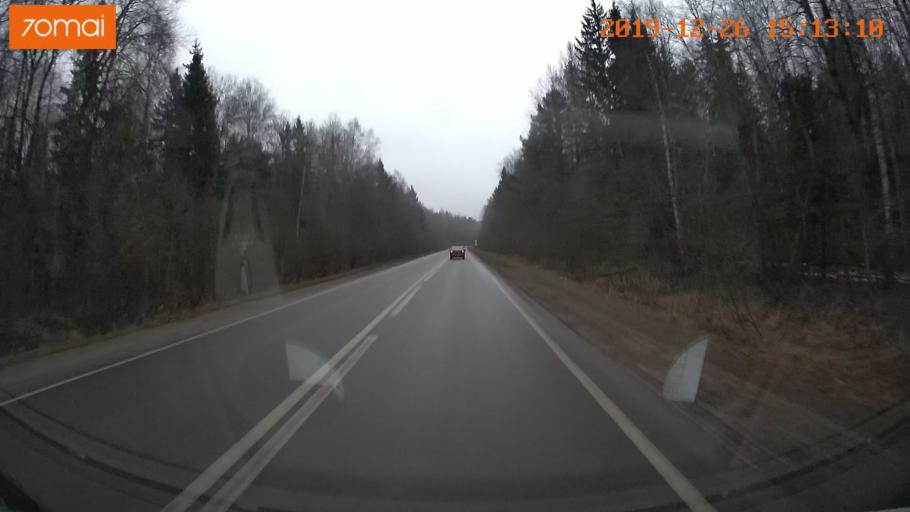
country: RU
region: Jaroslavl
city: Rybinsk
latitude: 58.1197
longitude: 38.8833
